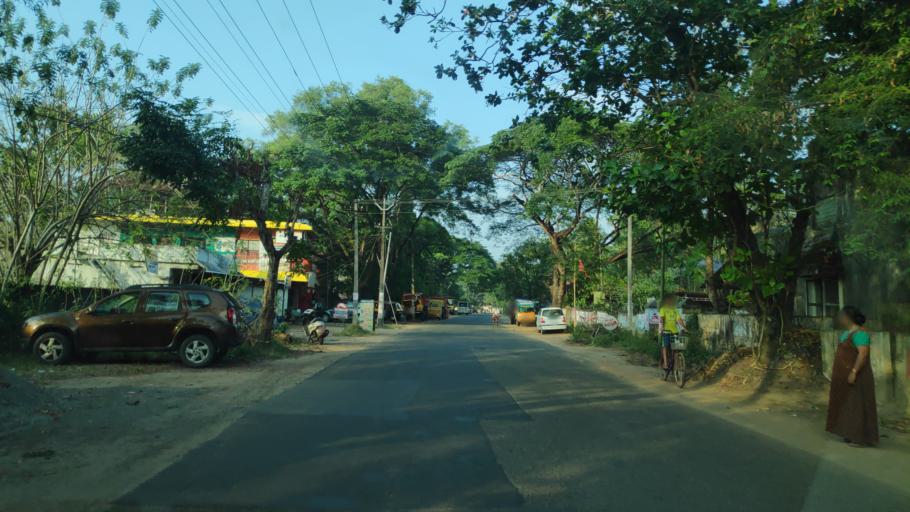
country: IN
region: Kerala
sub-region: Alappuzha
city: Shertallai
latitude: 9.6128
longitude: 76.3625
